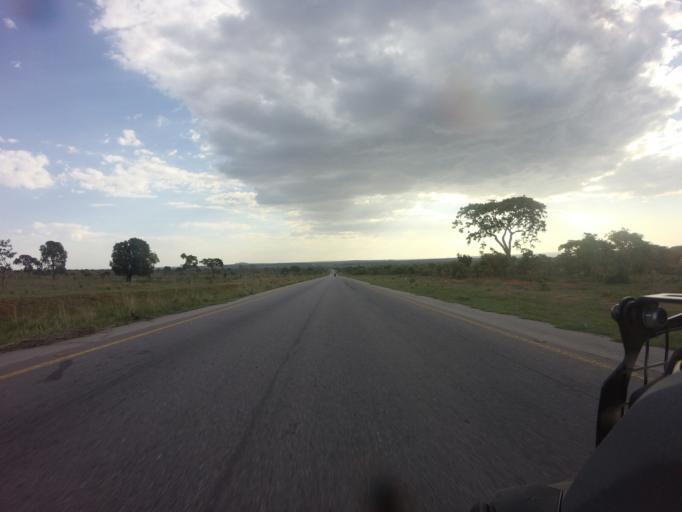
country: AO
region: Huila
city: Lubango
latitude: -14.5420
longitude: 14.0831
